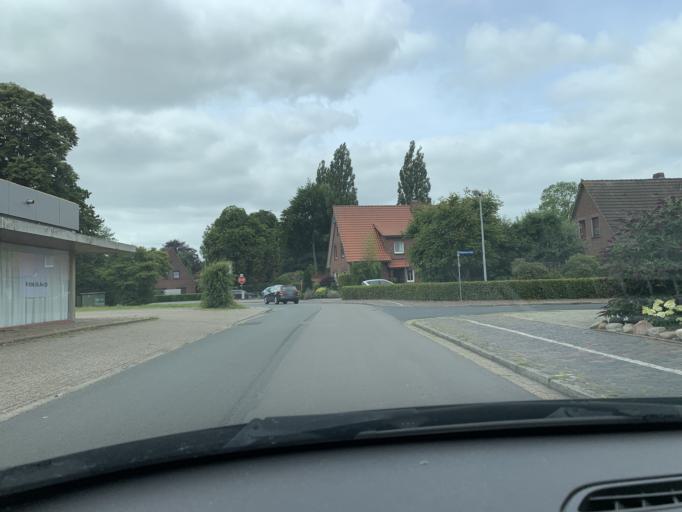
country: DE
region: Lower Saxony
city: Westerstede
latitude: 53.2612
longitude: 7.9329
